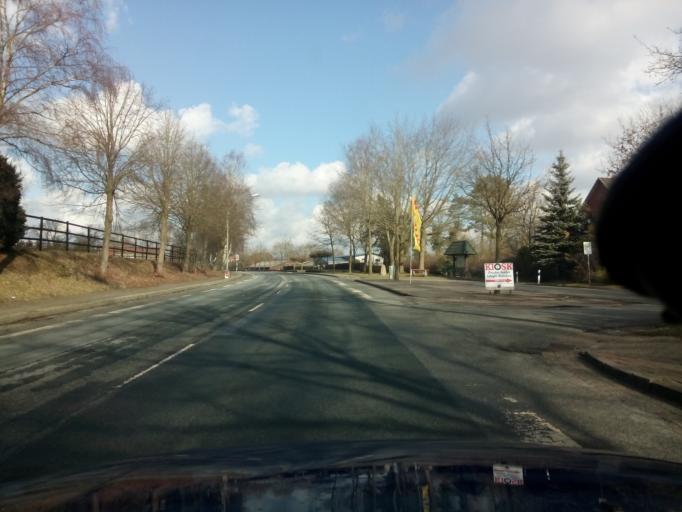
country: DE
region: Lower Saxony
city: Gnarrenburg
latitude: 53.3824
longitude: 8.9650
